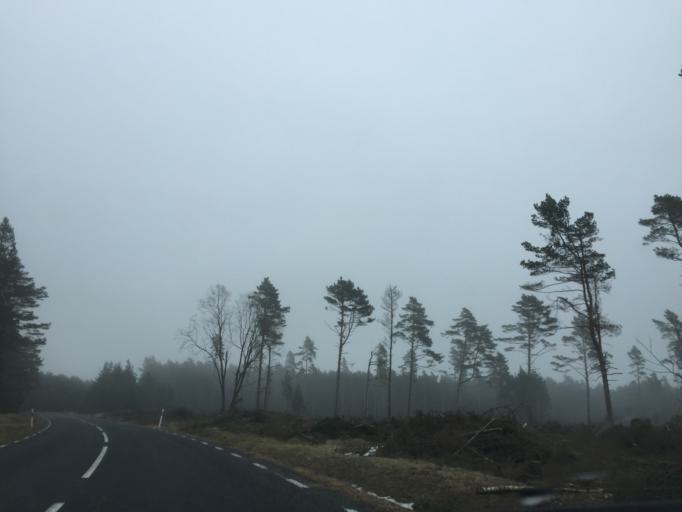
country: EE
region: Saare
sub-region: Kuressaare linn
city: Kuressaare
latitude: 58.4678
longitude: 22.0223
